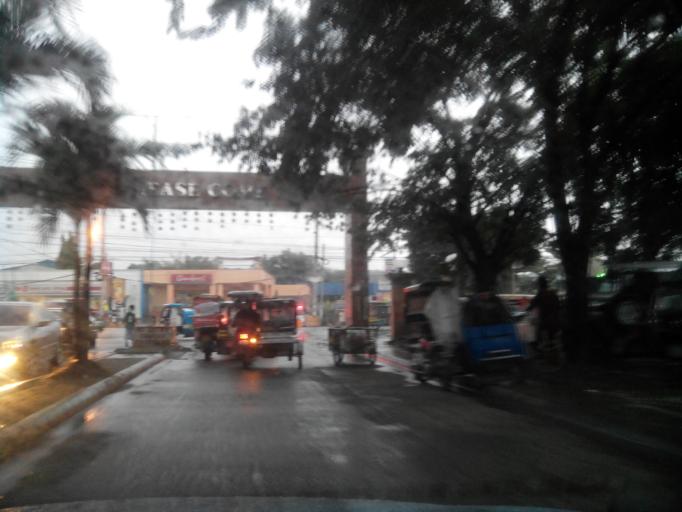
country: PH
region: Calabarzon
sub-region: Province of Rizal
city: Taytay
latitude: 14.5576
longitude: 121.1358
